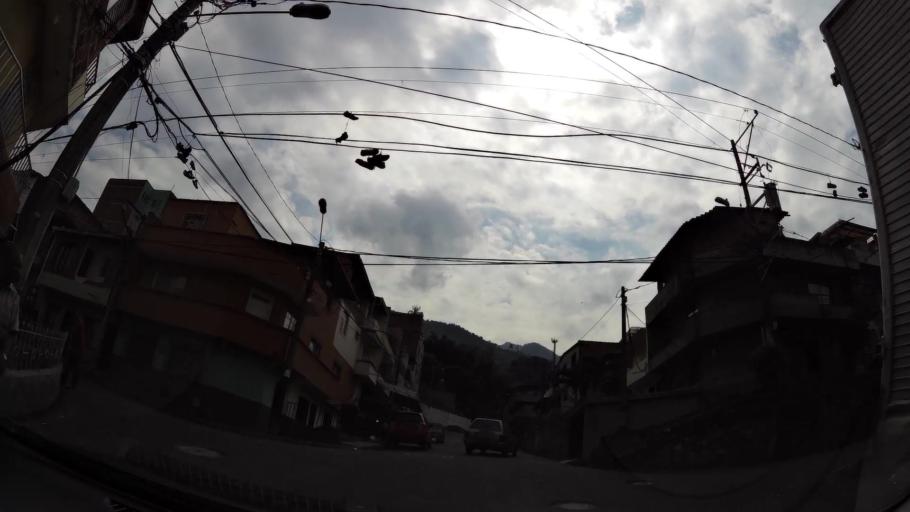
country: CO
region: Antioquia
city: Medellin
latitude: 6.2794
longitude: -75.5515
